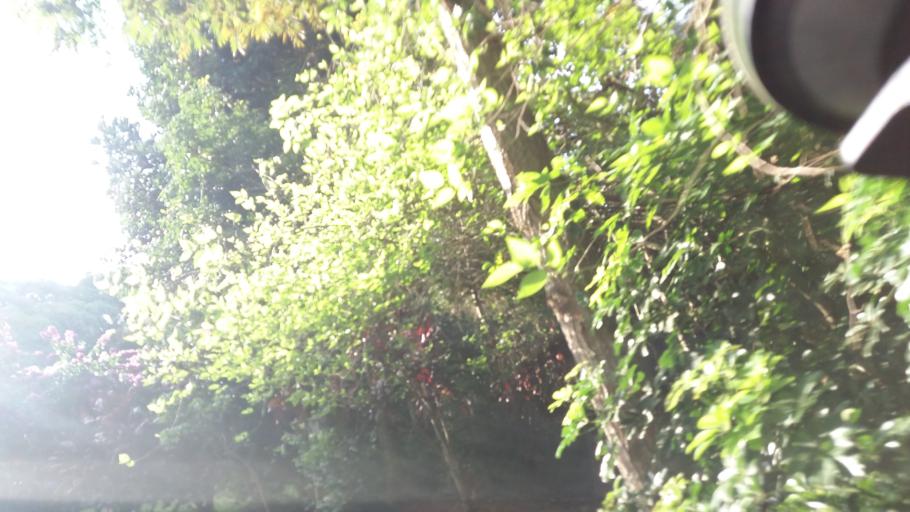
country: BR
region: Sao Paulo
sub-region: Bom Jesus Dos Perdoes
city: Bom Jesus dos Perdoes
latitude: -23.1684
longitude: -46.4623
